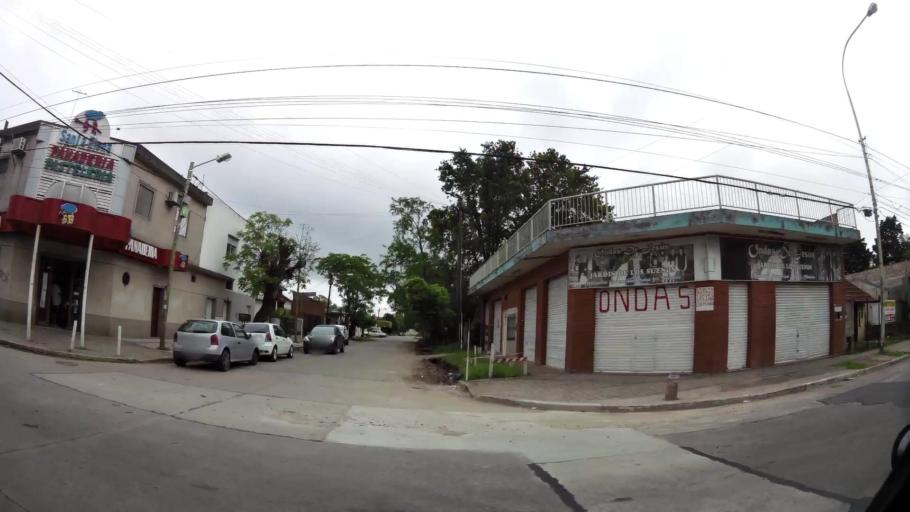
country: AR
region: Buenos Aires
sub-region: Partido de Quilmes
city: Quilmes
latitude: -34.7777
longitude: -58.2395
